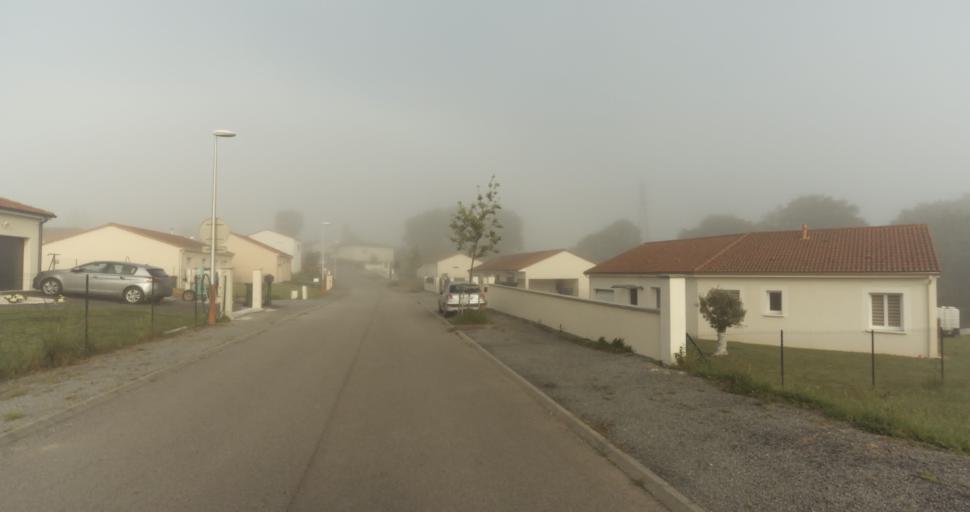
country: FR
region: Limousin
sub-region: Departement de la Haute-Vienne
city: Condat-sur-Vienne
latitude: 45.7840
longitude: 1.2783
